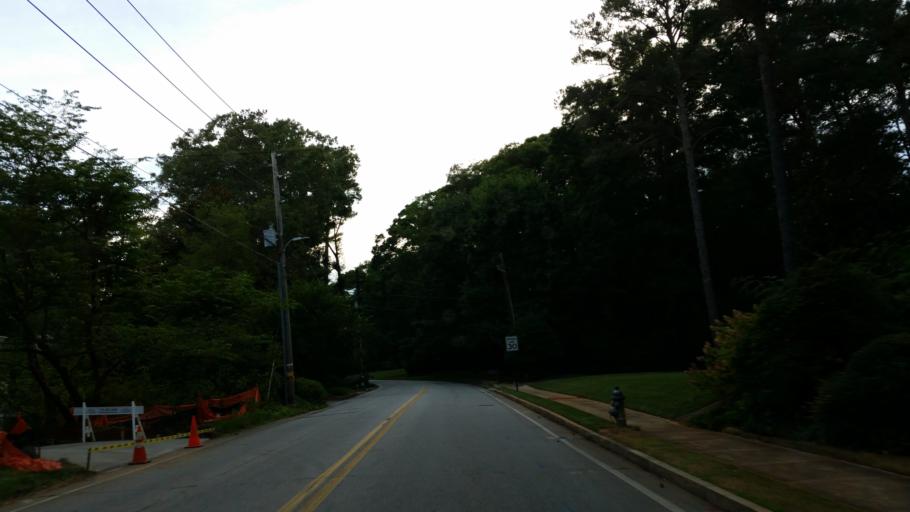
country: US
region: Georgia
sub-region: DeKalb County
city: North Atlanta
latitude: 33.8481
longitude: -84.3912
